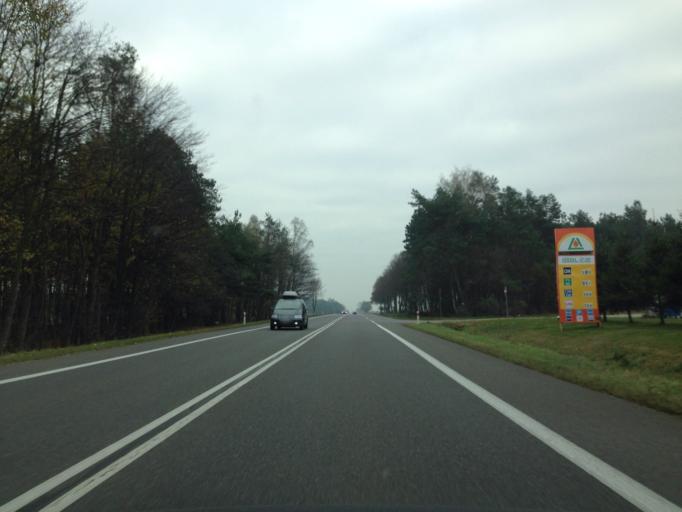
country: PL
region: Masovian Voivodeship
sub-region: Powiat plocki
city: Starozreby
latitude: 52.6655
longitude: 20.0741
